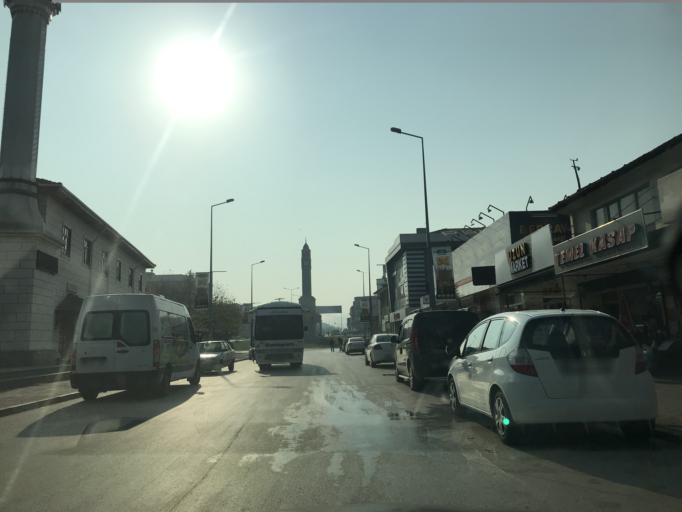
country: TR
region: Duzce
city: Cumayeri
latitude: 40.8742
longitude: 30.9504
